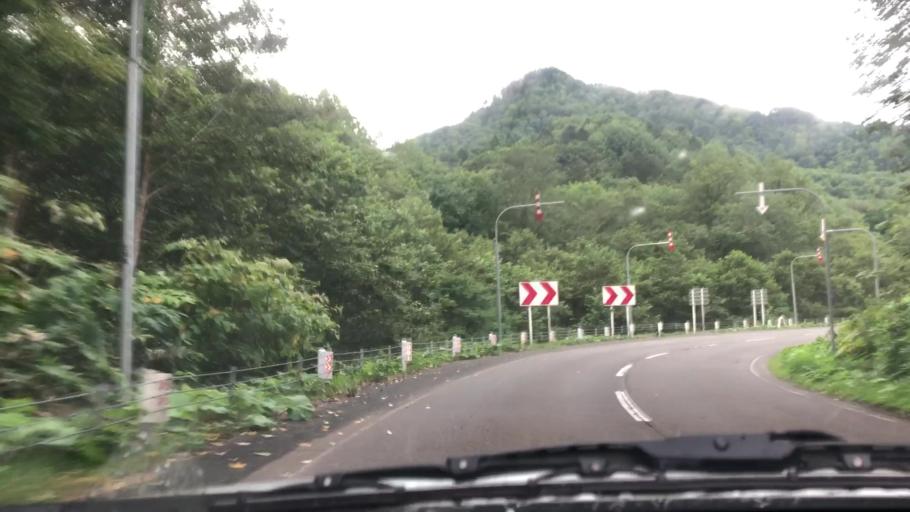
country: JP
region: Hokkaido
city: Shimo-furano
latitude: 42.9159
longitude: 142.3749
